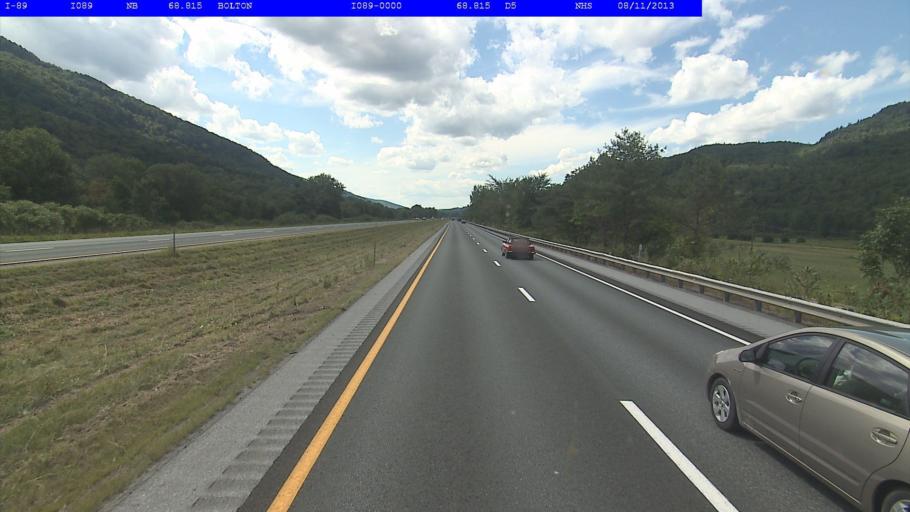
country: US
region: Vermont
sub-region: Washington County
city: Waterbury
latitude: 44.3640
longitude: -72.8458
